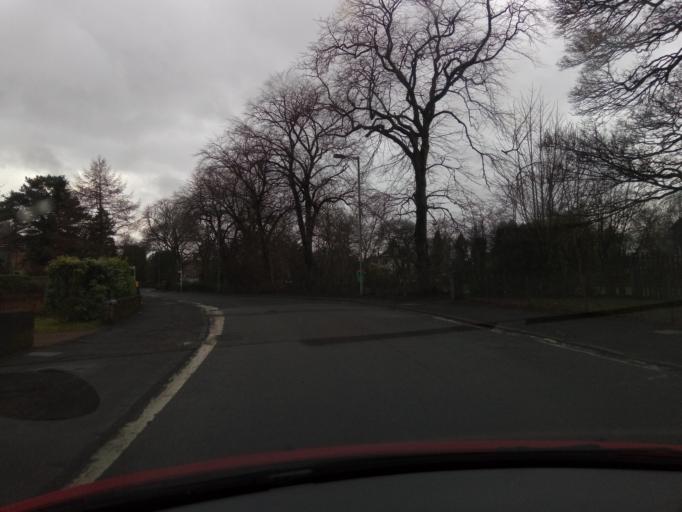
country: GB
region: Scotland
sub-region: East Dunbartonshire
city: Kirkintilloch
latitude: 55.9268
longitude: -4.1550
